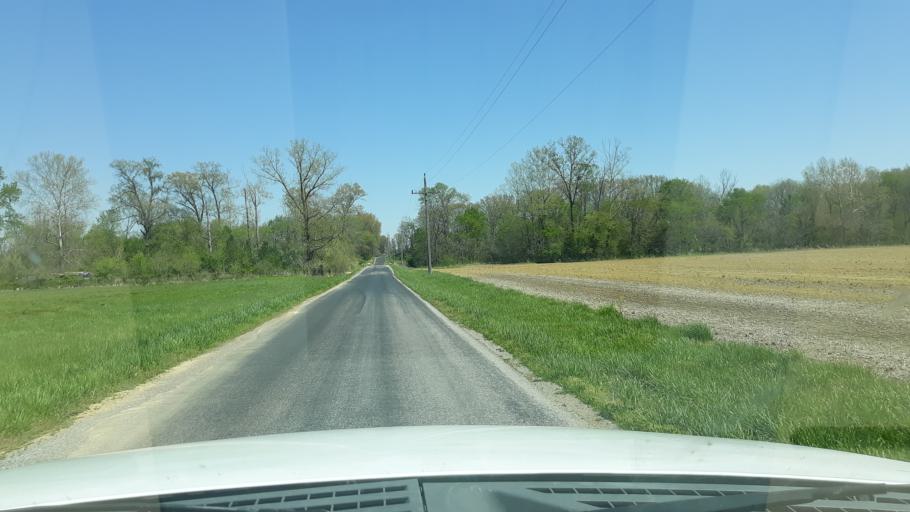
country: US
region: Illinois
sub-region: Saline County
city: Harrisburg
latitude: 37.8341
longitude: -88.6211
